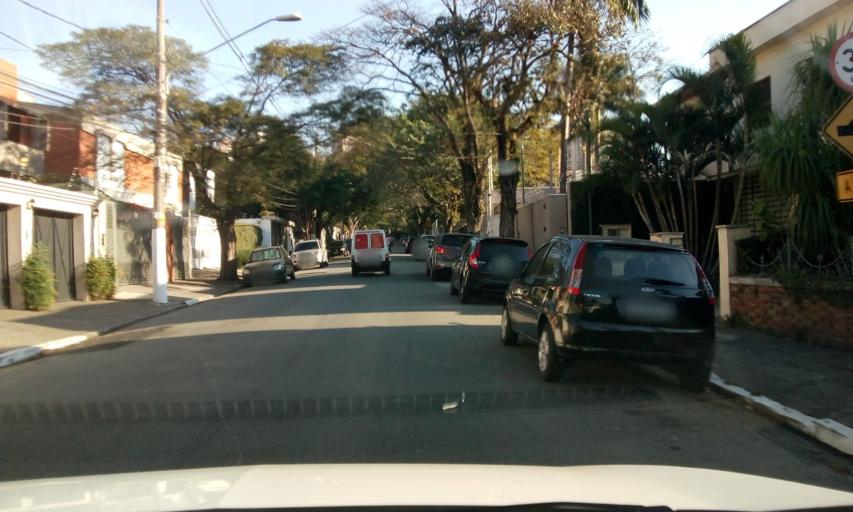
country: BR
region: Sao Paulo
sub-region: Sao Paulo
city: Sao Paulo
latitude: -23.5883
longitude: -46.6655
